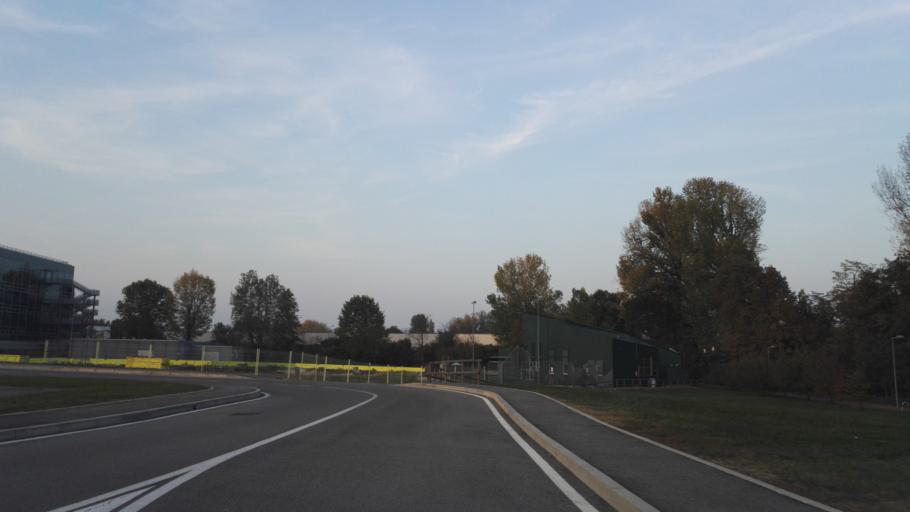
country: IT
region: Lombardy
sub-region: Citta metropolitana di Milano
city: San Bovio-San Felice
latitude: 45.4592
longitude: 9.3105
